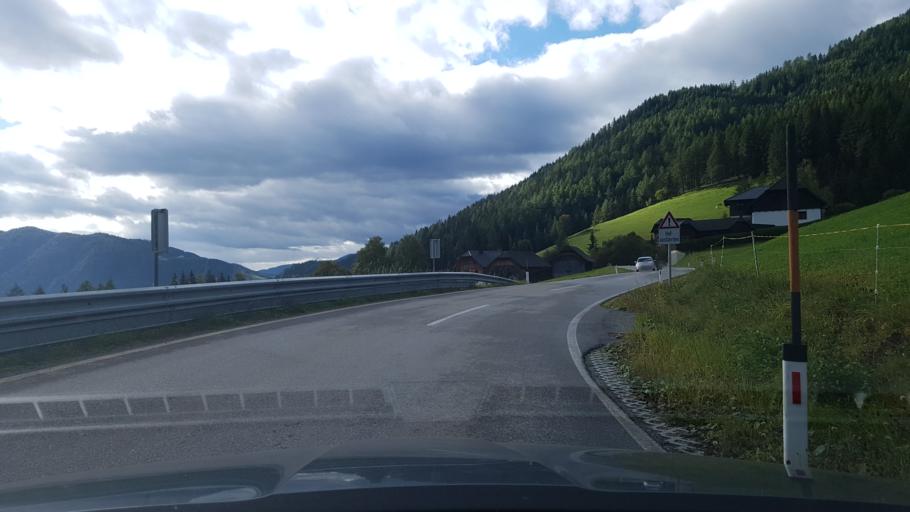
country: AT
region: Styria
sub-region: Politischer Bezirk Murau
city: Schoder
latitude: 47.2079
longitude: 14.1081
